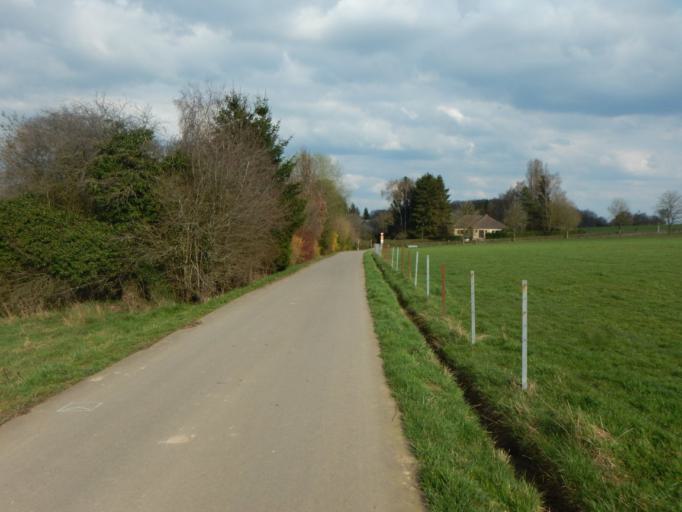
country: LU
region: Grevenmacher
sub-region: Canton d'Echternach
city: Beaufort
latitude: 49.8162
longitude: 6.2796
